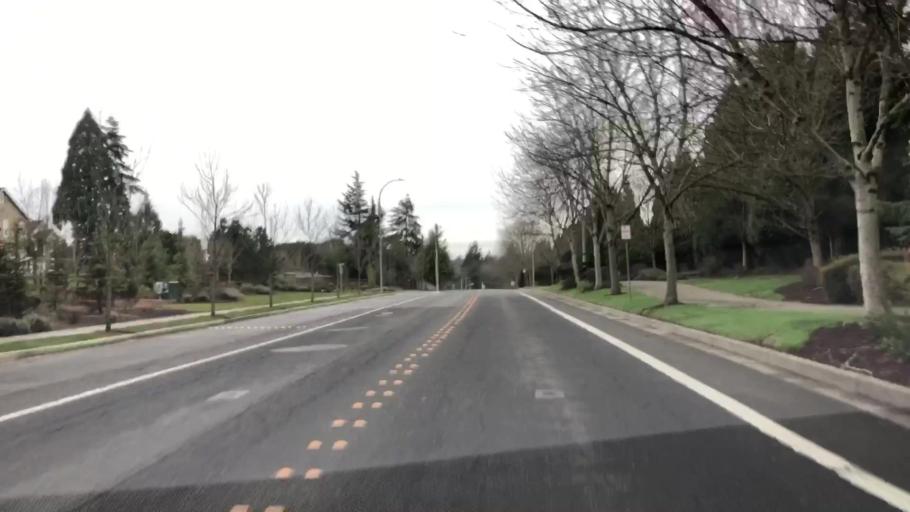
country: US
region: Washington
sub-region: King County
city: Redmond
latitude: 47.7040
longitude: -122.1276
